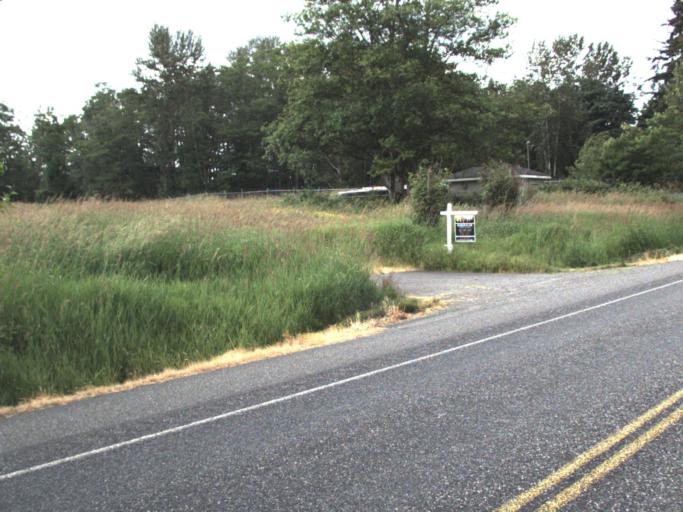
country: US
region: Washington
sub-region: Whatcom County
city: Ferndale
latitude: 48.8917
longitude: -122.6446
